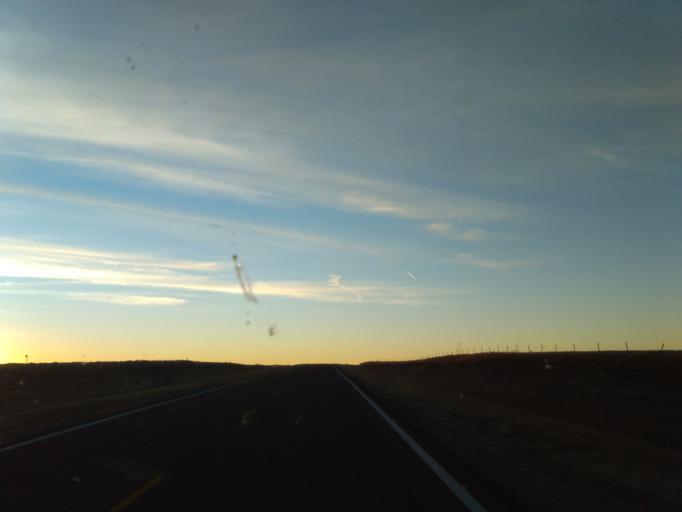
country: US
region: Kansas
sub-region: Wallace County
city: Sharon Springs
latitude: 38.9013
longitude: -101.8156
